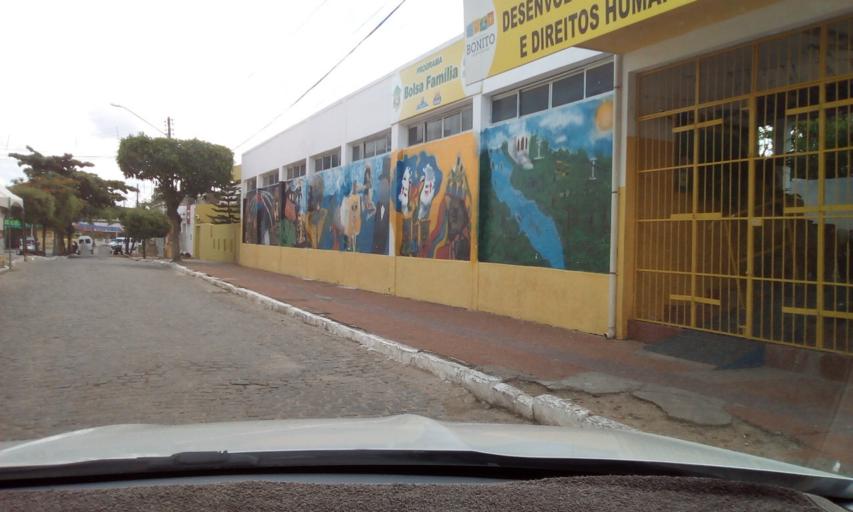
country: BR
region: Pernambuco
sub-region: Bonito
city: Bonito
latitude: -8.4713
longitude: -35.7295
